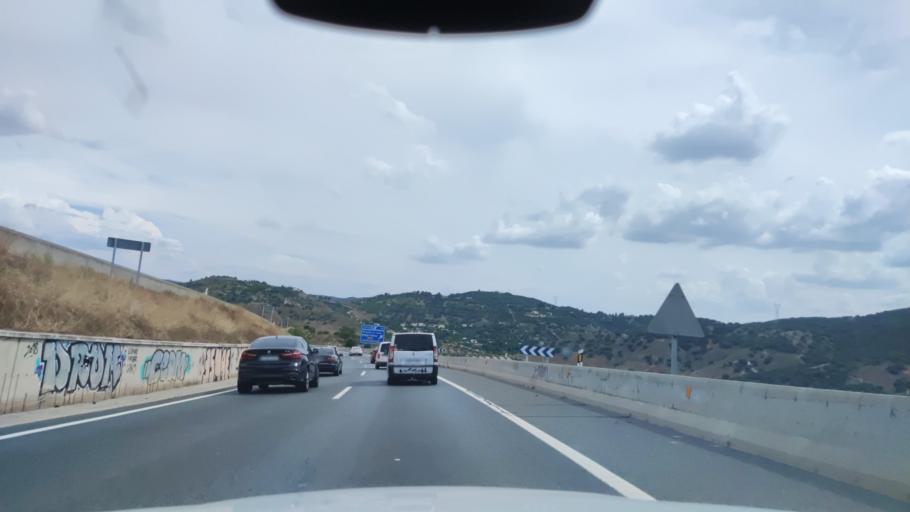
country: ES
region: Madrid
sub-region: Provincia de Madrid
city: Perales de Tajuna
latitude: 40.2337
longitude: -3.3446
